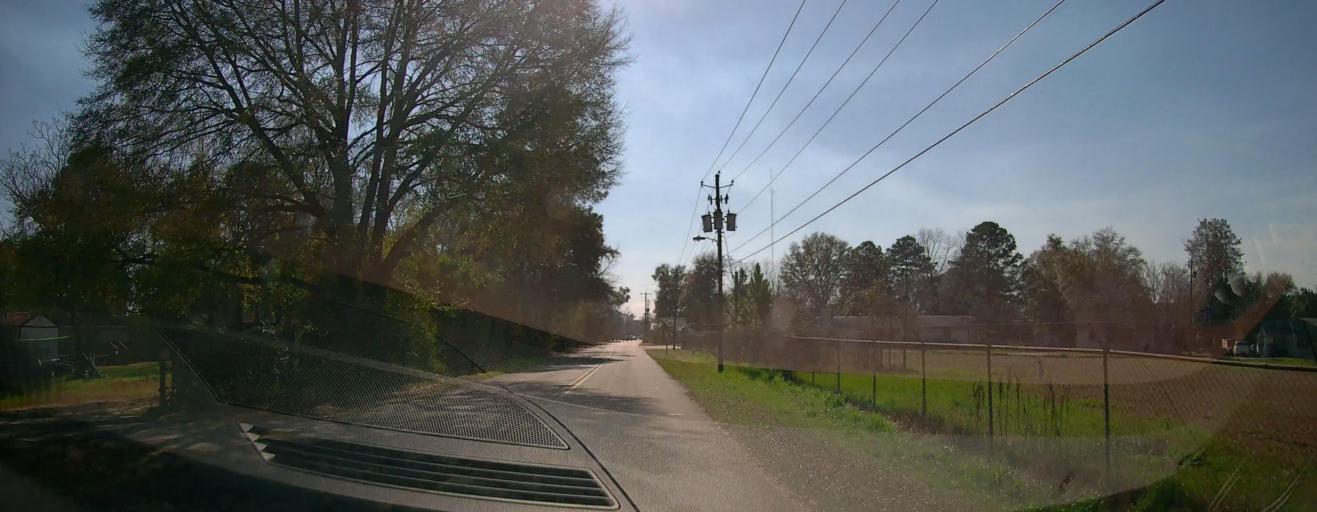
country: US
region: Georgia
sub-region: Macon County
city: Montezuma
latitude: 32.2894
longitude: -84.0103
